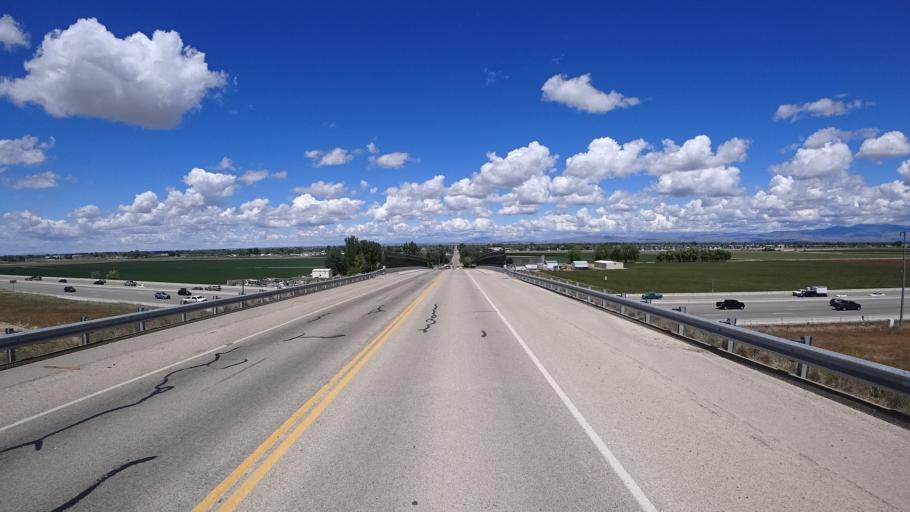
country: US
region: Idaho
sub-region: Ada County
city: Meridian
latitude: 43.5941
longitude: -116.4536
